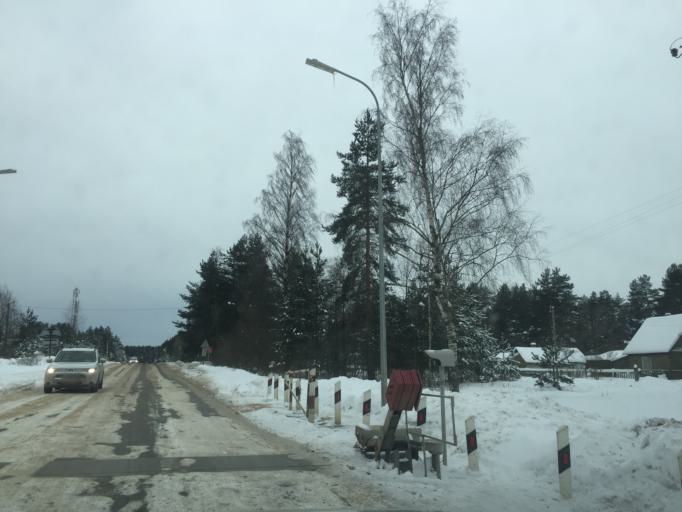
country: RU
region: Leningrad
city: Imeni Sverdlova
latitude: 59.8642
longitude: 30.6711
